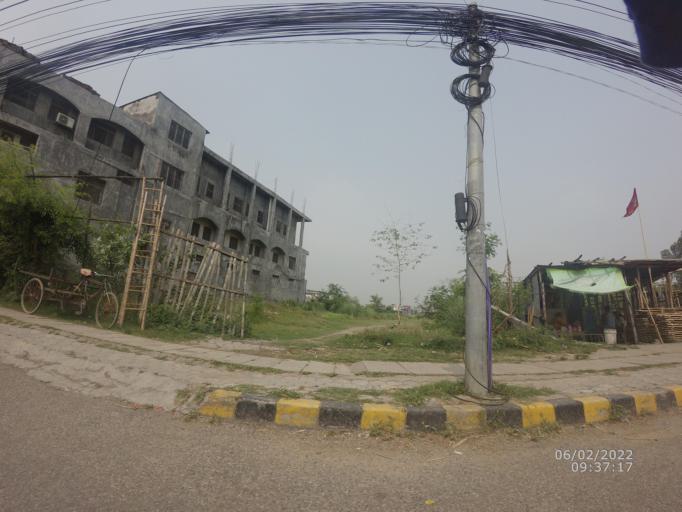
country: NP
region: Western Region
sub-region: Lumbini Zone
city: Bhairahawa
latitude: 27.4983
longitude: 83.4583
